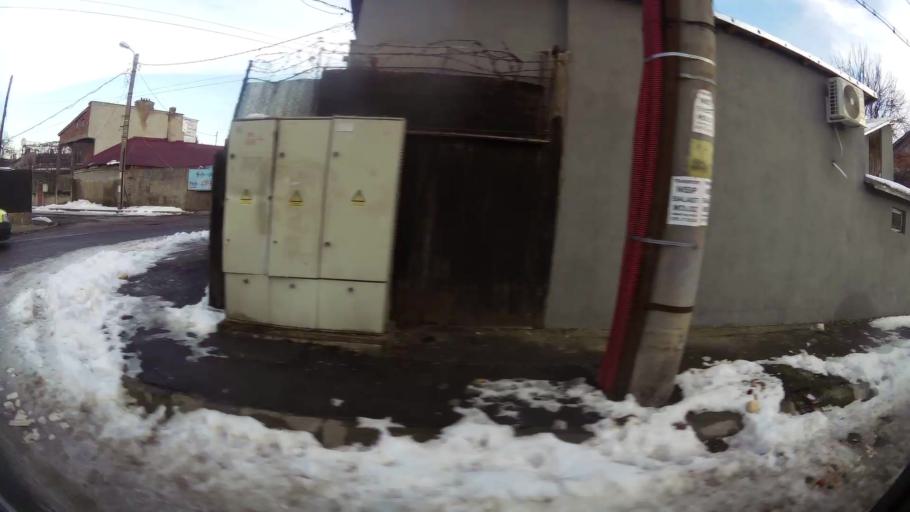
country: RO
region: Bucuresti
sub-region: Municipiul Bucuresti
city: Bucuresti
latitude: 44.3933
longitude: 26.0753
